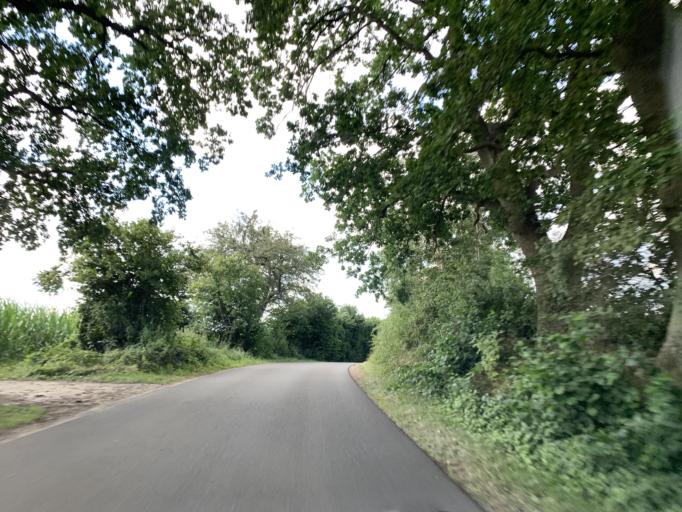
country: DE
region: Mecklenburg-Vorpommern
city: Carpin
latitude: 53.3716
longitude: 13.2584
